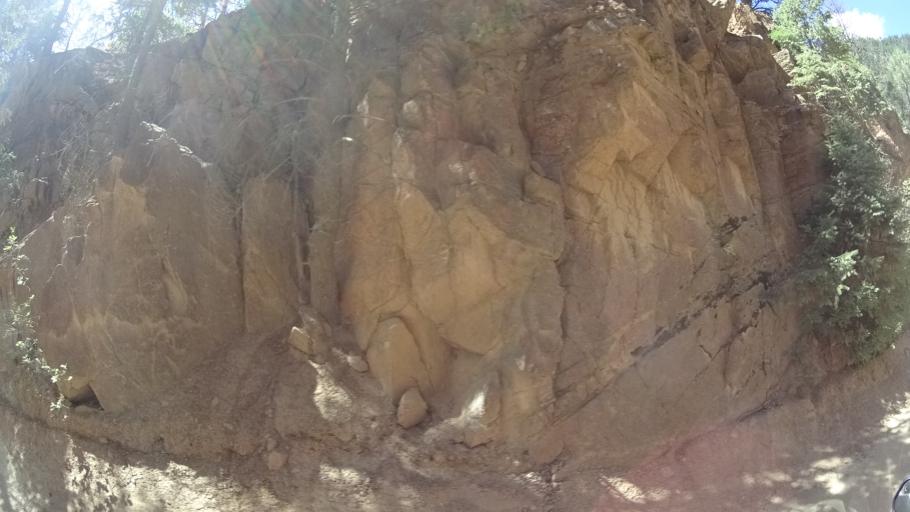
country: US
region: Colorado
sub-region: El Paso County
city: Manitou Springs
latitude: 38.7946
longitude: -104.8964
